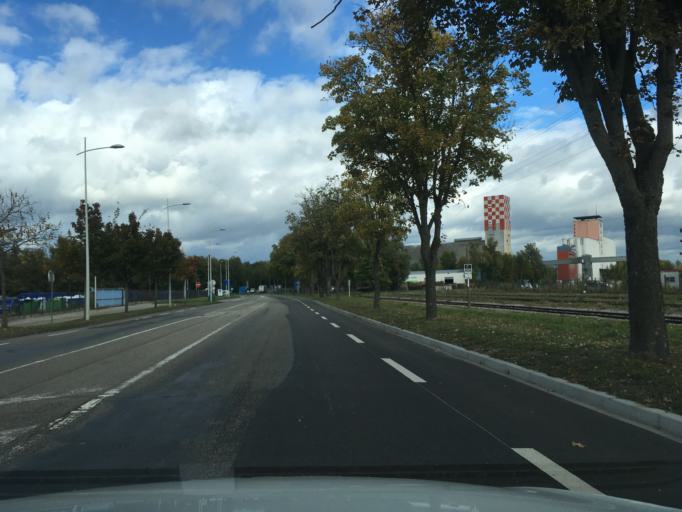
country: DE
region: Baden-Wuerttemberg
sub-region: Freiburg Region
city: Kehl
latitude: 48.5424
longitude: 7.7886
